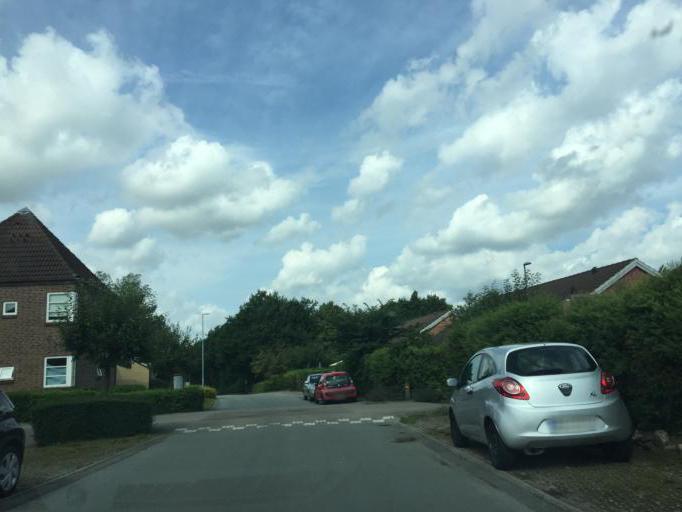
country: DK
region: South Denmark
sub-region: Odense Kommune
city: Hojby
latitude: 55.3351
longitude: 10.4434
